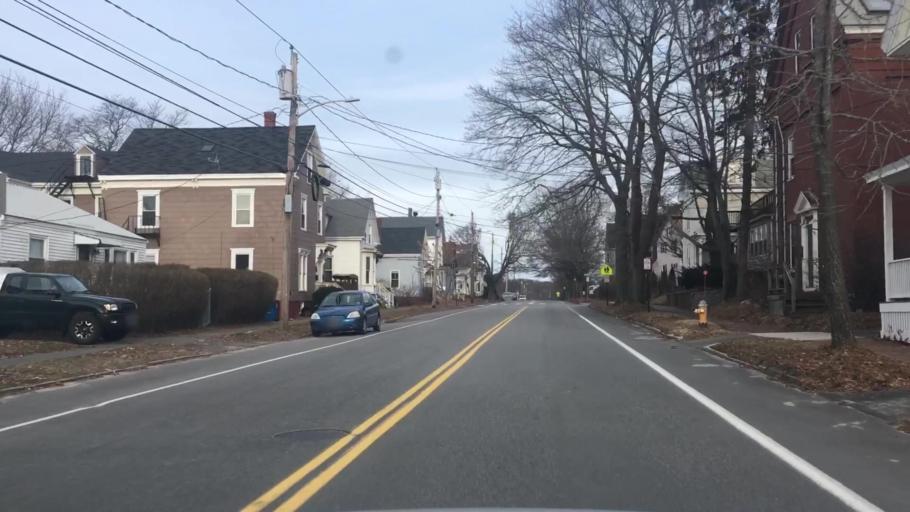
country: US
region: Maine
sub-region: Cumberland County
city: Portland
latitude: 43.6587
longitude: -70.2822
